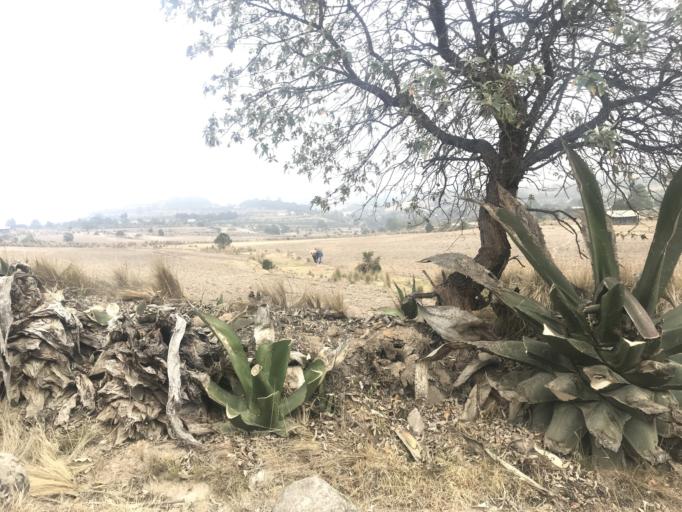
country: MX
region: Puebla
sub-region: Zautla
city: San Andres Yahuitlalpan
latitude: 19.6872
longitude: -97.7923
